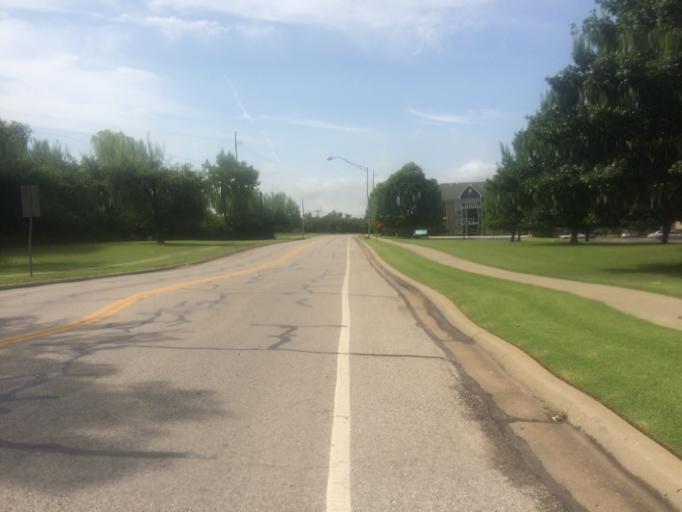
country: US
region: Oklahoma
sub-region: Cleveland County
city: Norman
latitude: 35.1891
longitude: -97.4243
